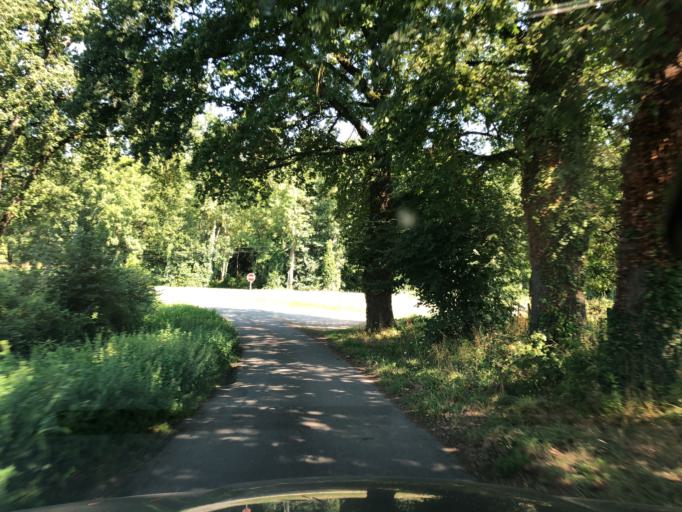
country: FR
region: Auvergne
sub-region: Departement de l'Allier
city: Cusset
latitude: 46.1362
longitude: 3.4773
